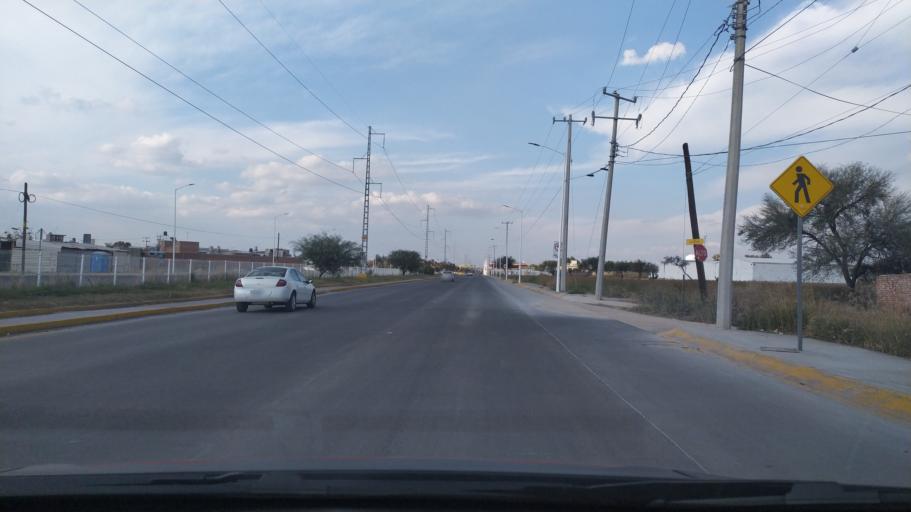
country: MX
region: Guanajuato
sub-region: Purisima del Rincon
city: Monte Grande
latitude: 21.0102
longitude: -101.8699
